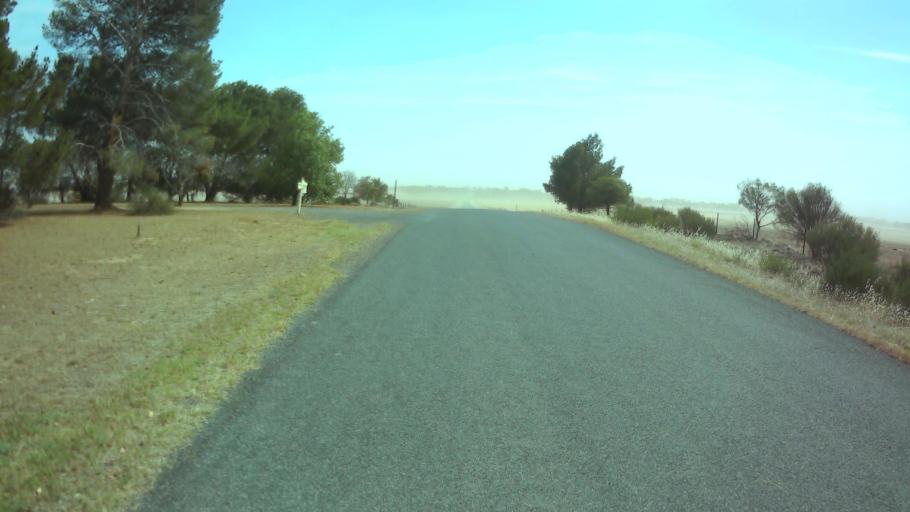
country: AU
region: New South Wales
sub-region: Weddin
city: Grenfell
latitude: -33.7304
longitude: 147.9981
